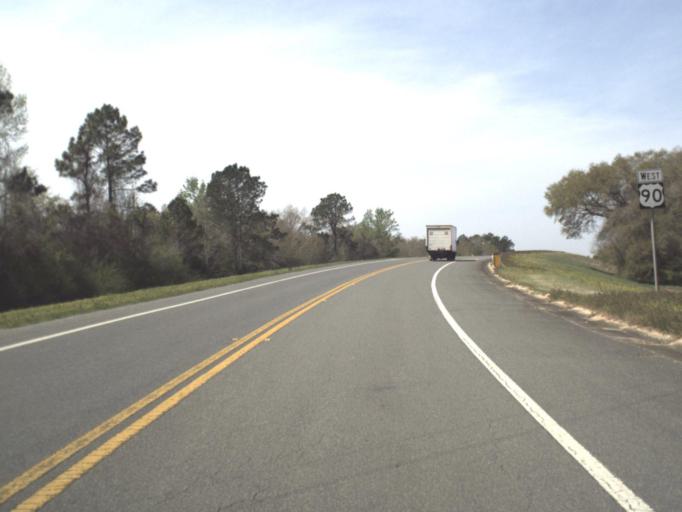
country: US
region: Florida
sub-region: Walton County
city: DeFuniak Springs
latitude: 30.7314
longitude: -85.9230
